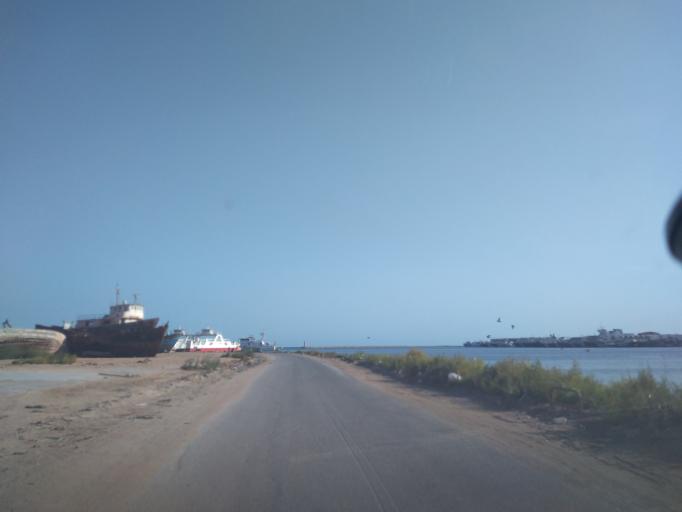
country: TN
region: Safaqis
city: Sfax
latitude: 34.7189
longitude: 10.7675
